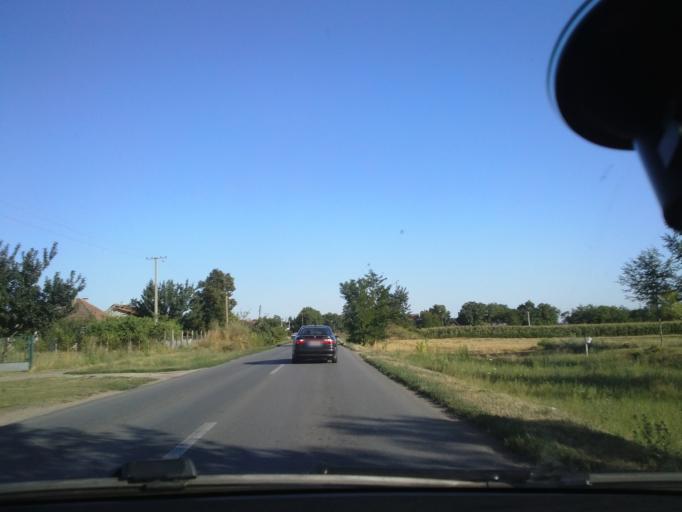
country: RS
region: Autonomna Pokrajina Vojvodina
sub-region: Zapadnobacki Okrug
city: Sombor
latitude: 45.7289
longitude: 19.1490
